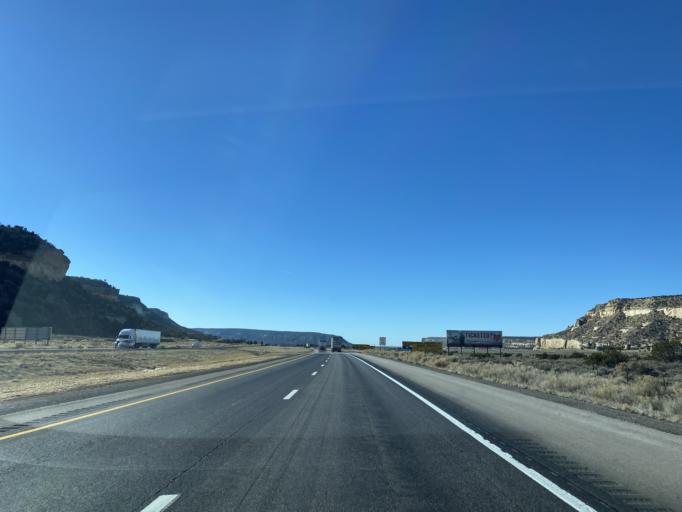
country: US
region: Arizona
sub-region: Apache County
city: Houck
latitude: 35.4115
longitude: -108.9975
